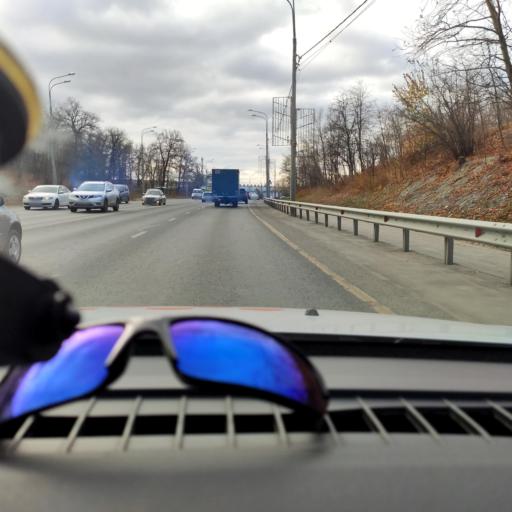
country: RU
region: Samara
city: Samara
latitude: 53.2812
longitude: 50.2288
